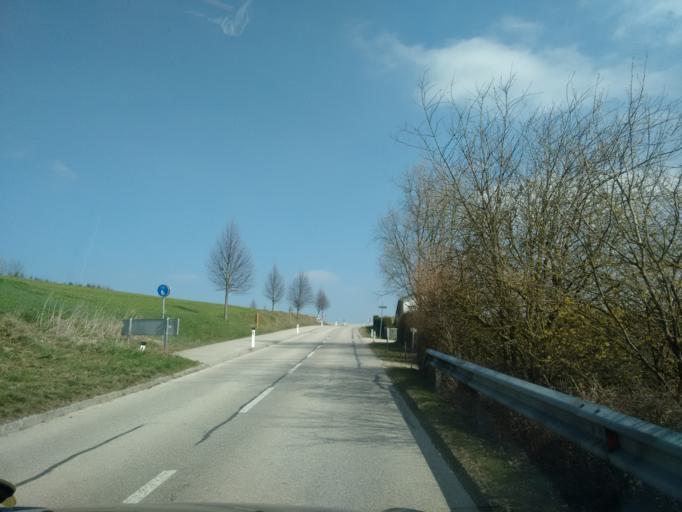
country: AT
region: Upper Austria
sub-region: Politischer Bezirk Grieskirchen
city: Bad Schallerbach
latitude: 48.2055
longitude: 13.9612
